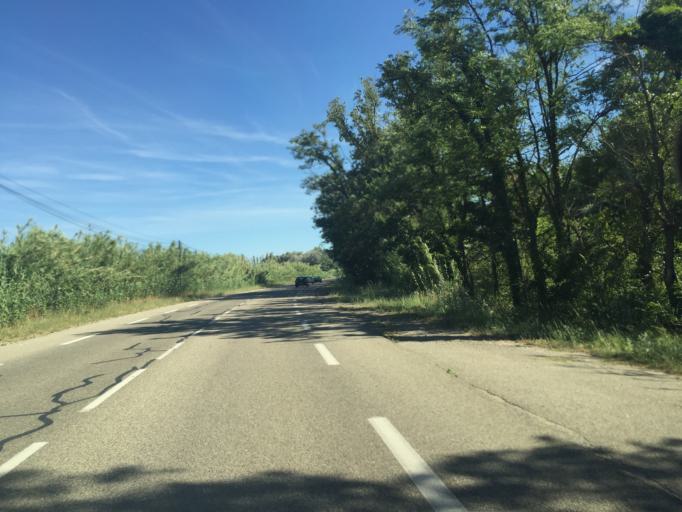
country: FR
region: Provence-Alpes-Cote d'Azur
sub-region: Departement du Vaucluse
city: Caderousse
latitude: 44.0955
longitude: 4.7619
